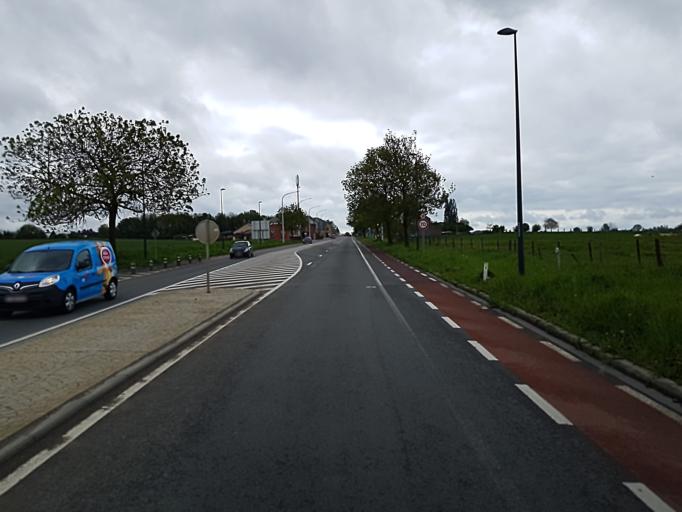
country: BE
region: Wallonia
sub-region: Province du Brabant Wallon
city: Chastre-Villeroux-Blanmont
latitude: 50.6320
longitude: 4.6536
